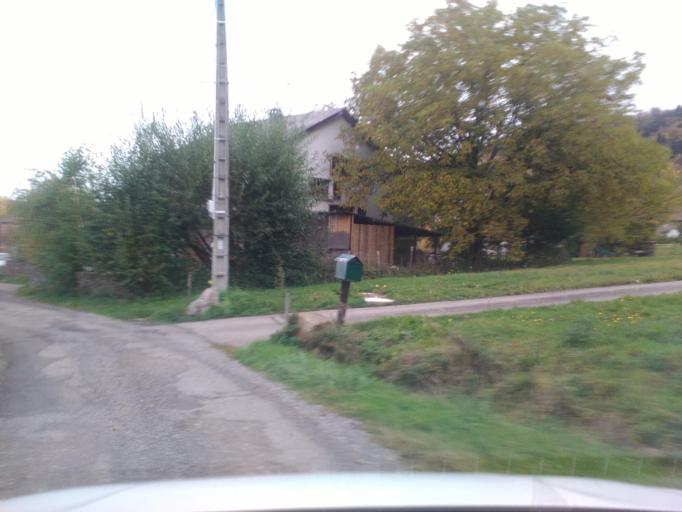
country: FR
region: Lorraine
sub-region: Departement des Vosges
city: Senones
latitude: 48.3324
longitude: 6.9930
